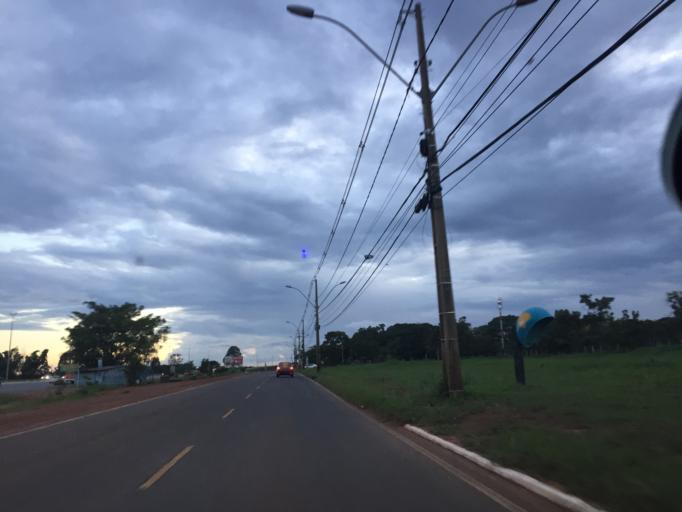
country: BR
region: Federal District
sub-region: Brasilia
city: Brasilia
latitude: -15.9010
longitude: -47.9635
